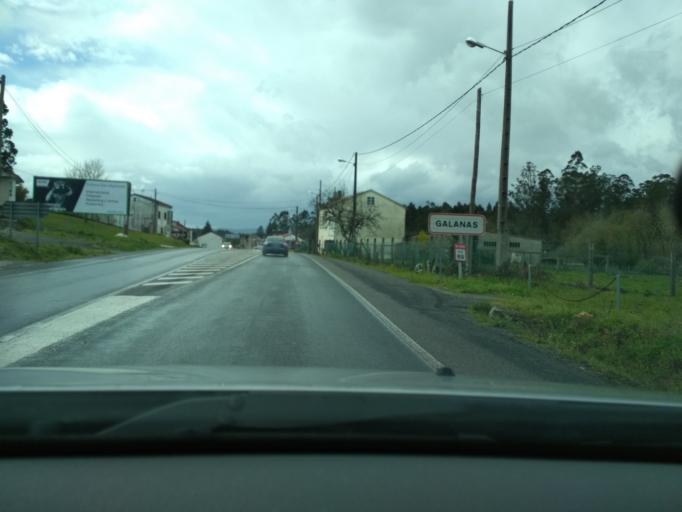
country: ES
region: Galicia
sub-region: Provincia da Coruna
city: Santiago de Compostela
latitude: 42.8361
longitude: -8.5870
